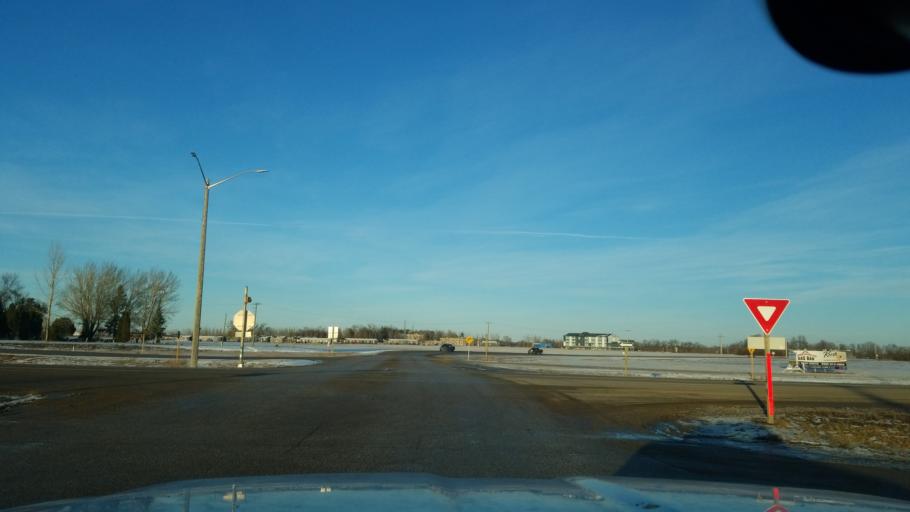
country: CA
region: Manitoba
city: Portage la Prairie
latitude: 49.9547
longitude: -98.3283
